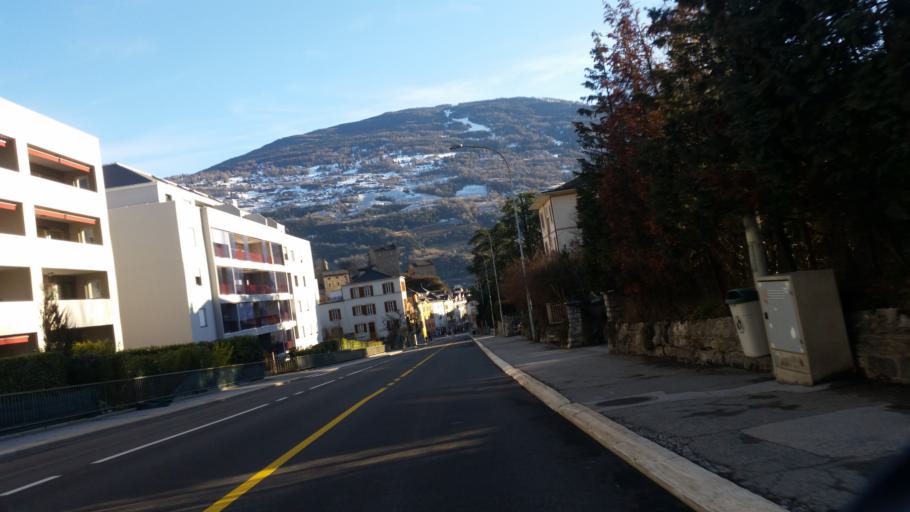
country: CH
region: Valais
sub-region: Sion District
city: Sitten
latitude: 46.2379
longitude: 7.3601
